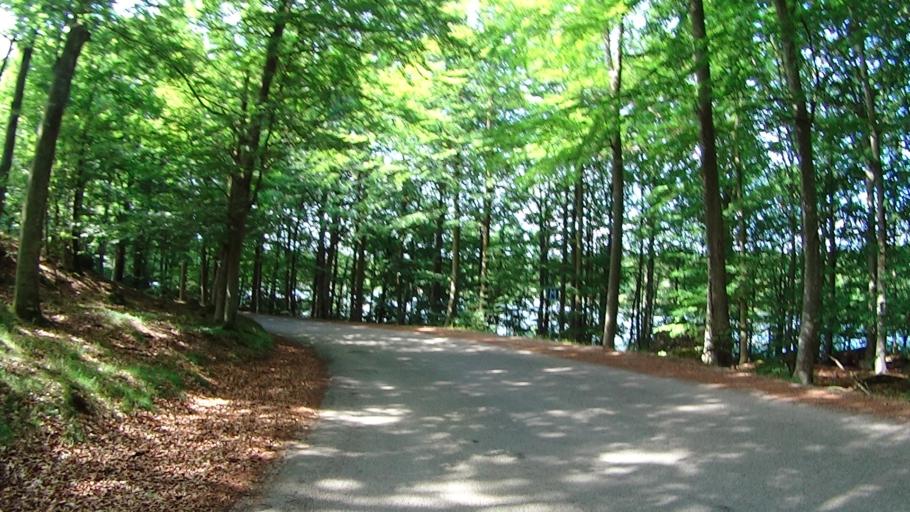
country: SE
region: Blekinge
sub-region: Ronneby Kommun
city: Brakne-Hoby
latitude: 56.1638
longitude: 15.0895
